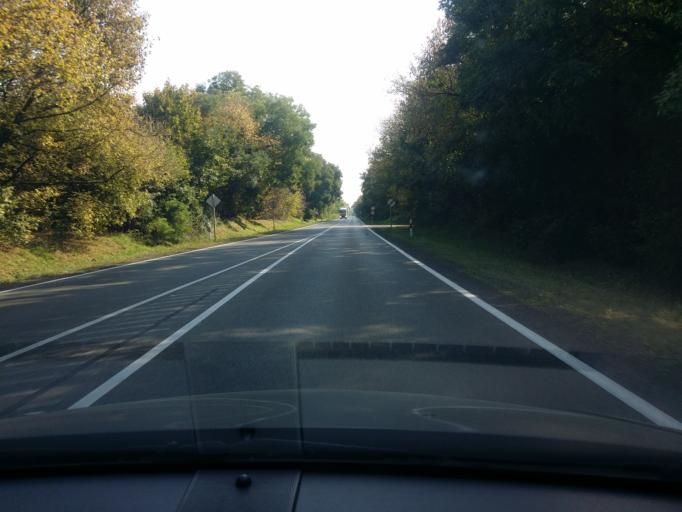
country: HU
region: Fejer
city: dunaujvaros
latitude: 46.9377
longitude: 18.9214
